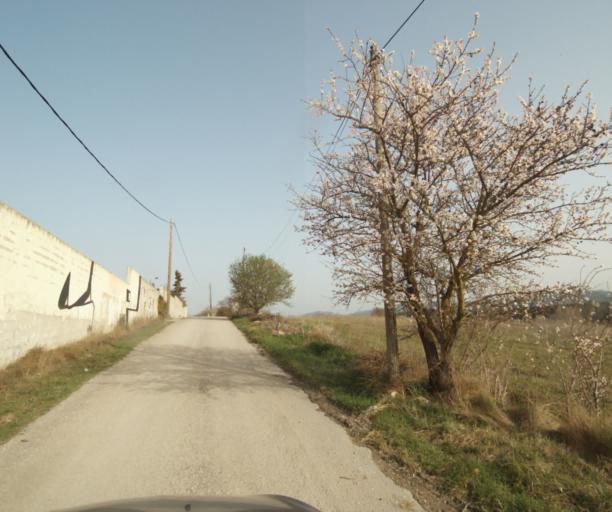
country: FR
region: Provence-Alpes-Cote d'Azur
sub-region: Departement des Bouches-du-Rhone
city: Septemes-les-Vallons
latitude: 43.4195
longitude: 5.3701
